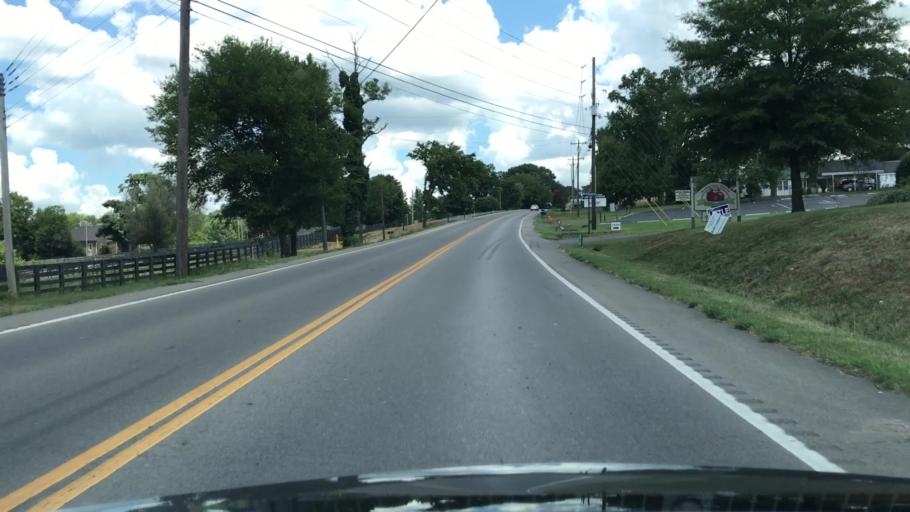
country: US
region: Tennessee
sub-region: Williamson County
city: Nolensville
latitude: 35.8954
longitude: -86.6663
